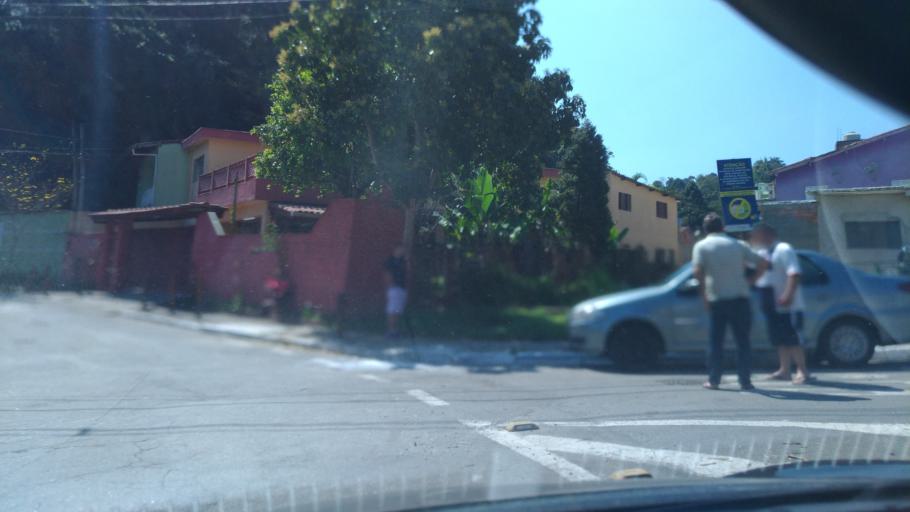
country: BR
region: Sao Paulo
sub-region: Sao Bernardo Do Campo
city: Sao Bernardo do Campo
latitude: -23.7753
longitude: -46.5208
